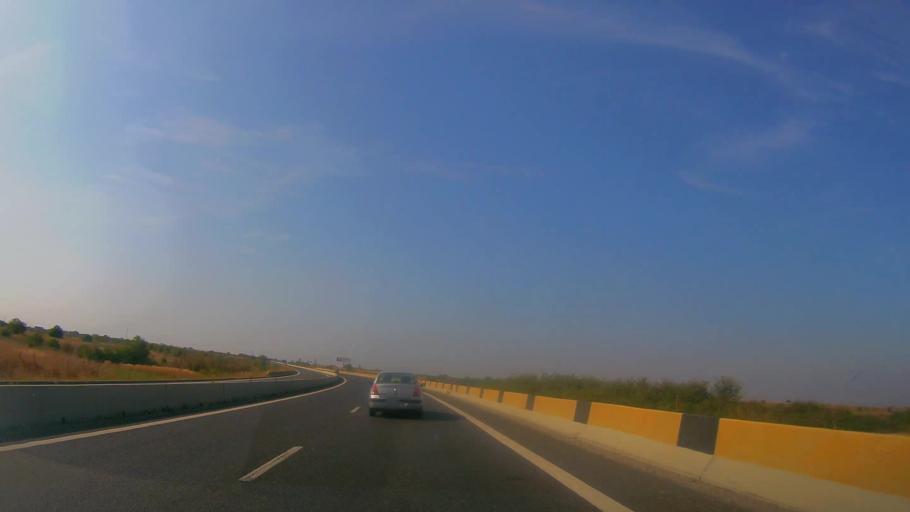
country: RO
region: Giurgiu
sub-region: Comuna Adunatii-Copaceni
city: Adunatii-Copaceni
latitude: 44.2622
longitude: 26.0426
